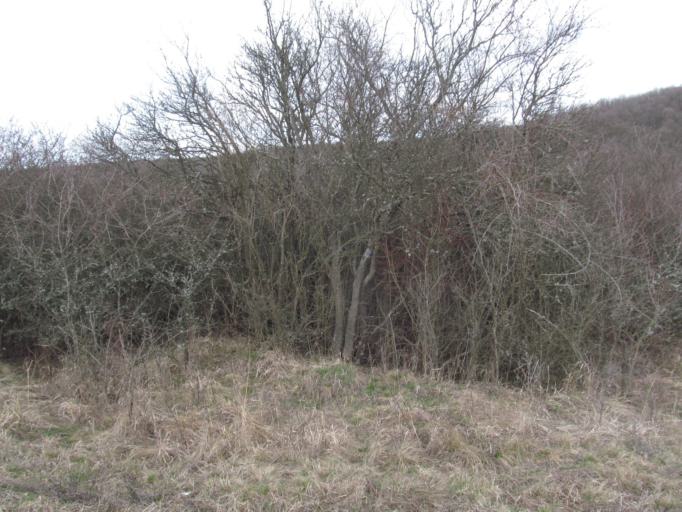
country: HU
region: Borsod-Abauj-Zemplen
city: Putnok
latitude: 48.4011
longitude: 20.4862
